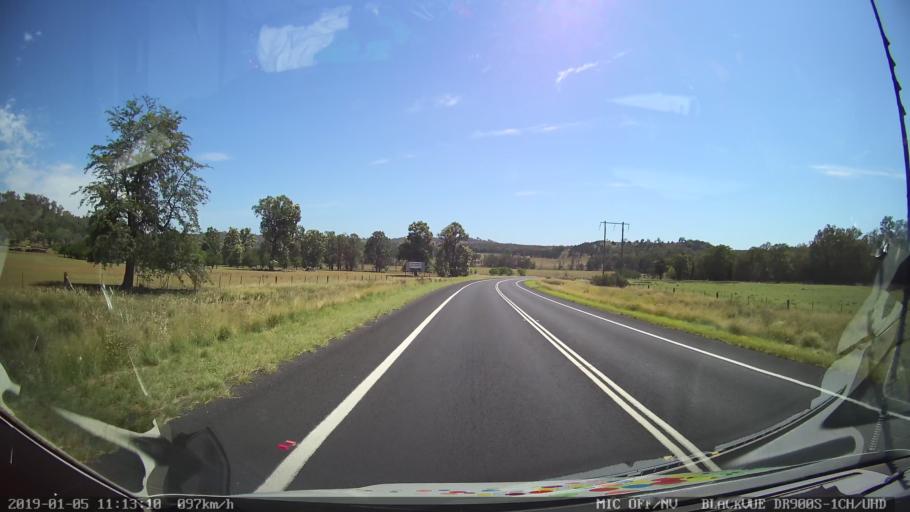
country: AU
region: New South Wales
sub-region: Warrumbungle Shire
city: Coonabarabran
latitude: -31.3736
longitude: 149.2676
